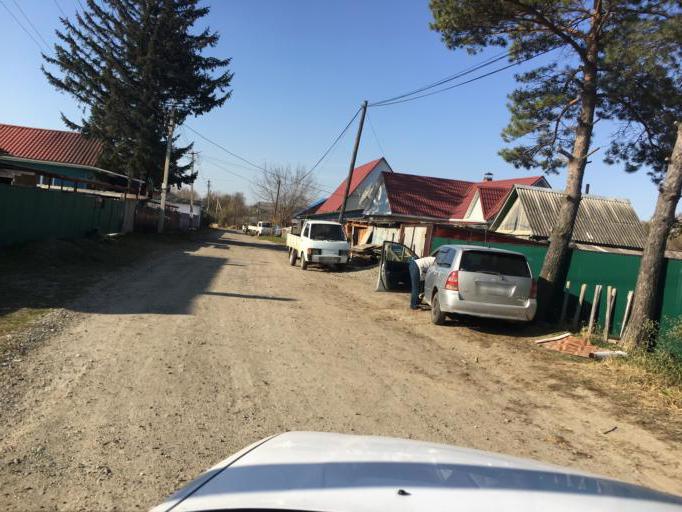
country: RU
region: Primorskiy
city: Dal'nerechensk
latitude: 45.9235
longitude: 133.7279
